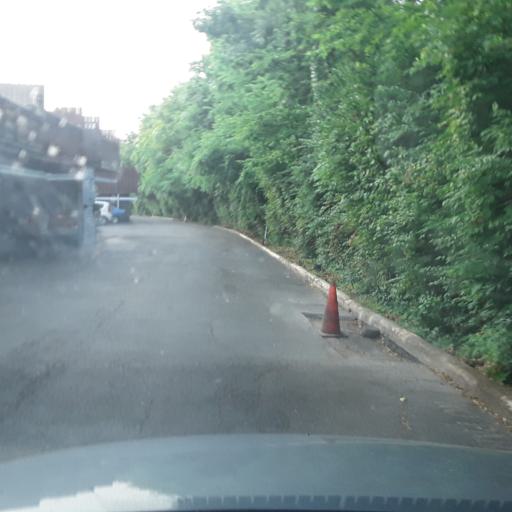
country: US
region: Tennessee
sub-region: Williamson County
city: Brentwood Estates
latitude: 36.0488
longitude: -86.7277
